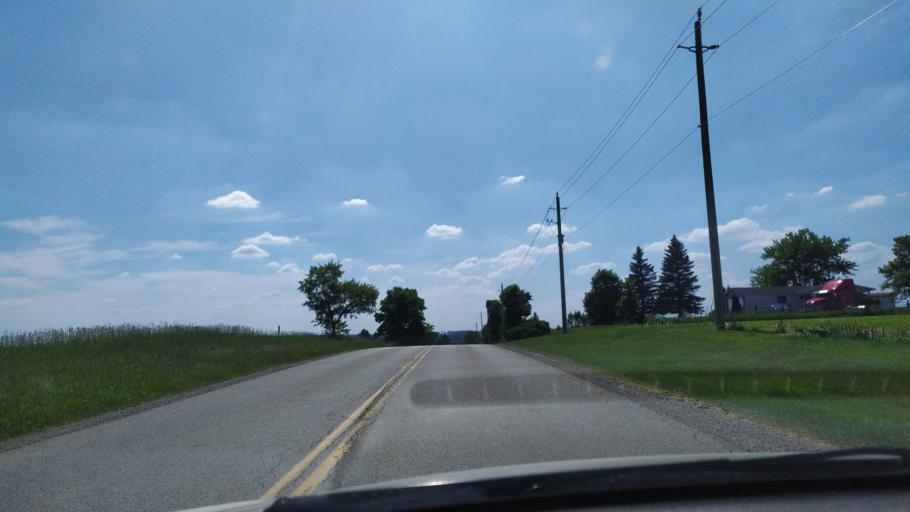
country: CA
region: Ontario
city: Kitchener
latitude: 43.3624
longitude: -80.6164
